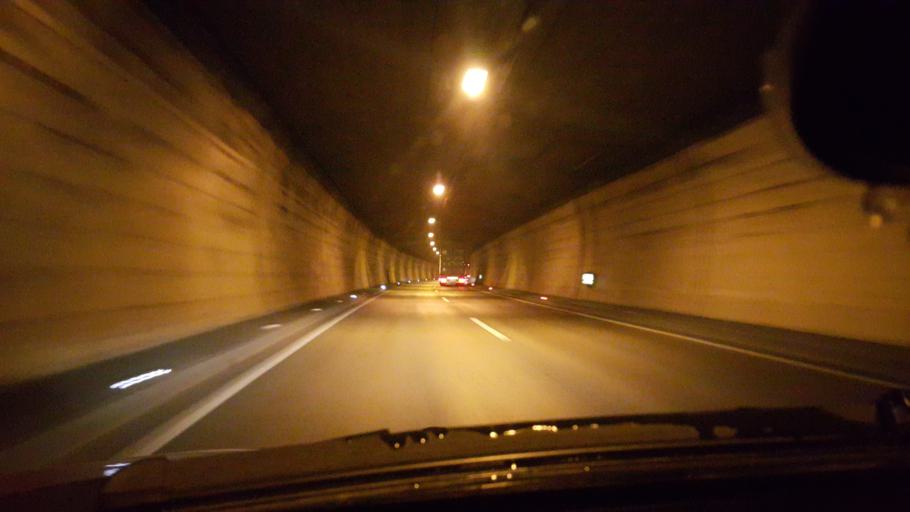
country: AT
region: Styria
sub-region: Graz Stadt
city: Wetzelsdorf
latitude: 47.0521
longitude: 15.3987
